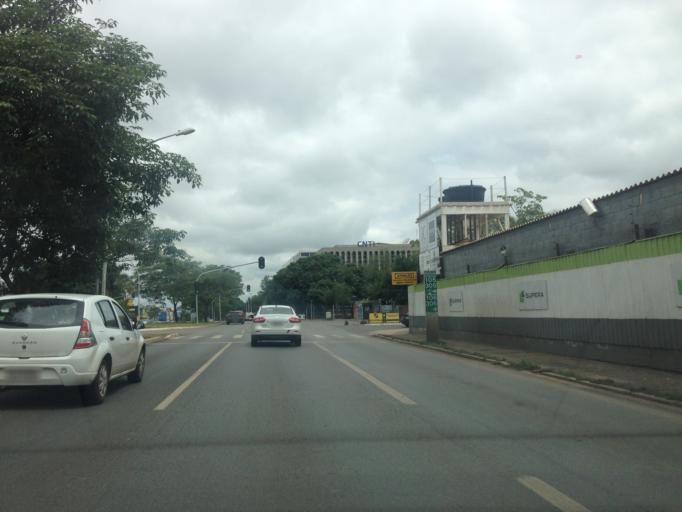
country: BR
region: Federal District
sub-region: Brasilia
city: Brasilia
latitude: -15.7755
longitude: -47.8880
